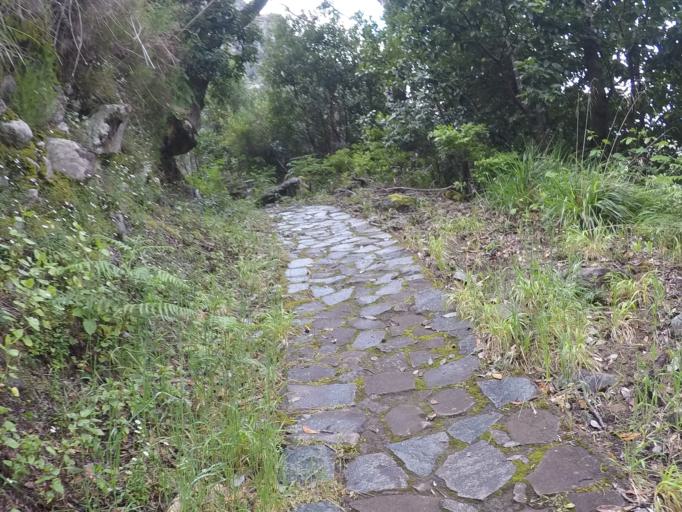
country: PT
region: Madeira
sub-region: Camara de Lobos
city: Curral das Freiras
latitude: 32.7476
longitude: -17.0053
